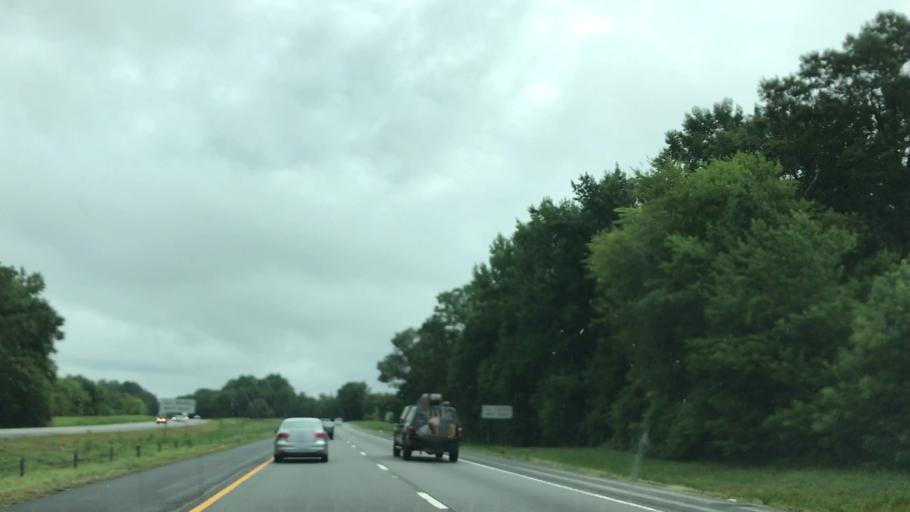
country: US
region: North Carolina
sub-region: Halifax County
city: Enfield
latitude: 36.1343
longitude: -77.7907
